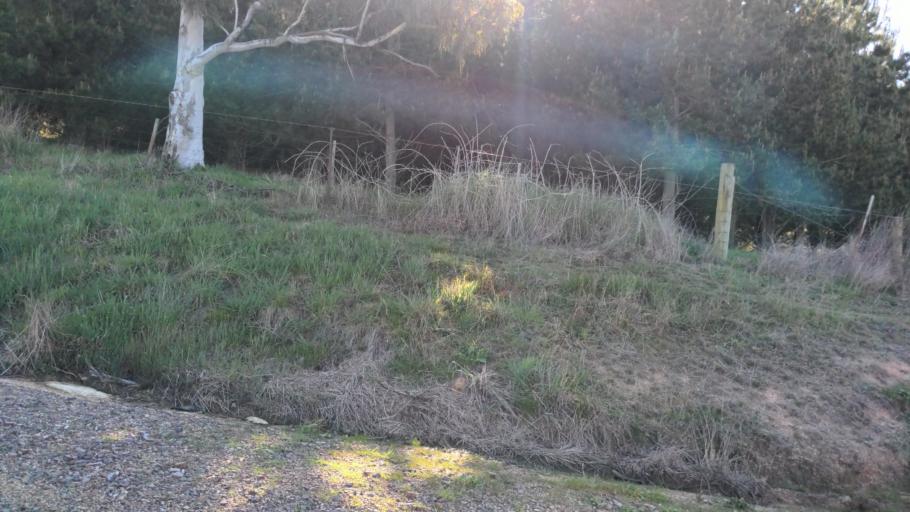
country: AU
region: New South Wales
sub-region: Blayney
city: Blayney
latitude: -33.4112
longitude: 149.3244
